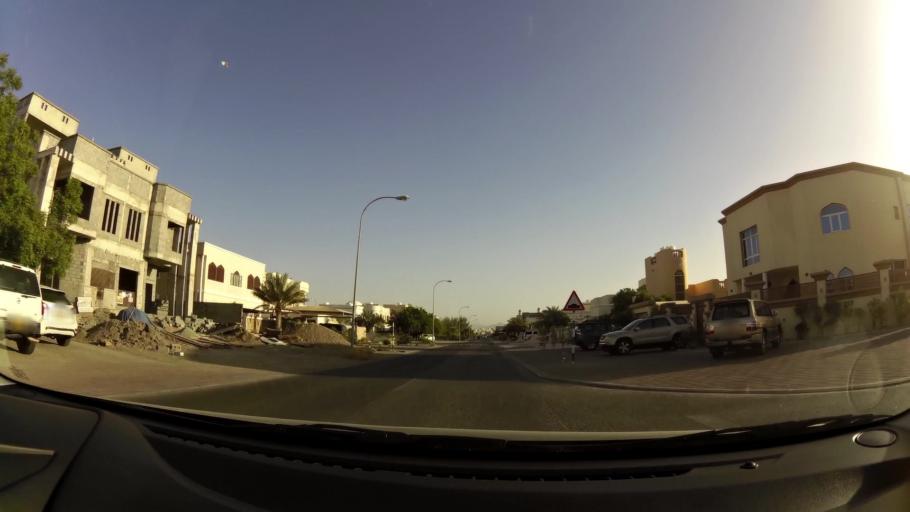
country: OM
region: Muhafazat Masqat
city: As Sib al Jadidah
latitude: 23.6110
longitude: 58.2203
